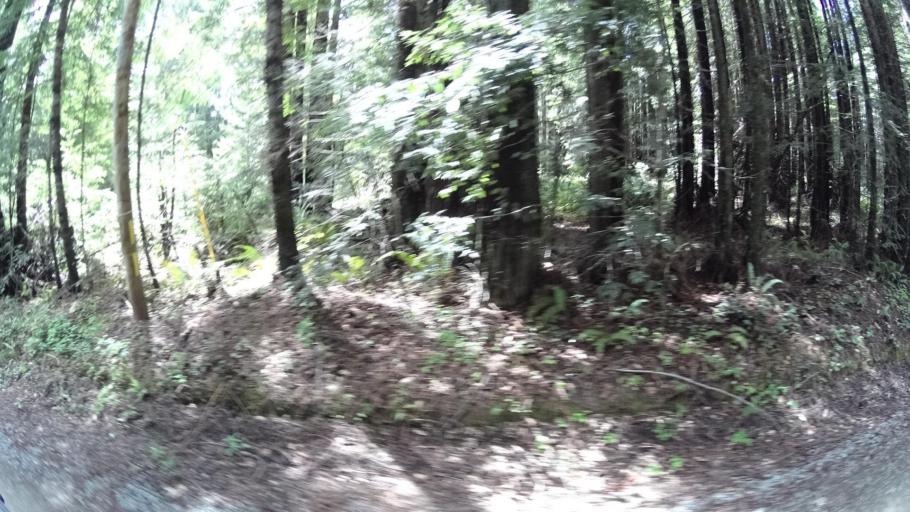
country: US
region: California
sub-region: Humboldt County
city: Blue Lake
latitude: 40.8047
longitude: -123.8825
